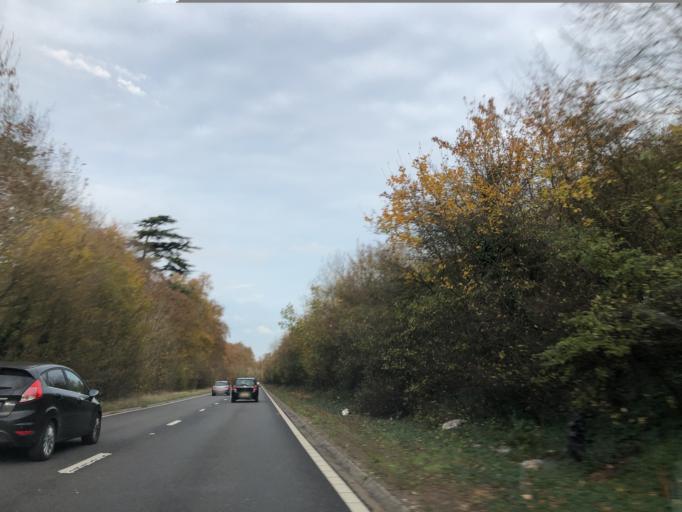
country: GB
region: England
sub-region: Royal Borough of Windsor and Maidenhead
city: Bisham
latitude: 51.5467
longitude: -0.7836
